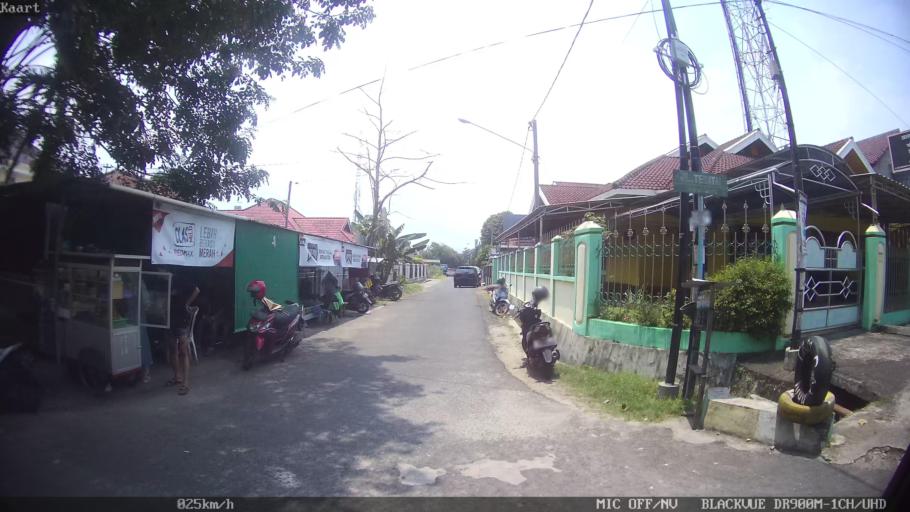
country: ID
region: Lampung
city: Bandarlampung
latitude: -5.4208
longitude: 105.2627
